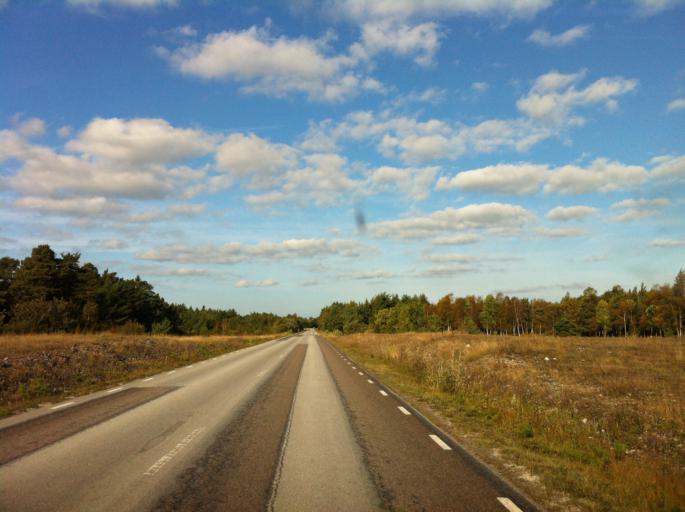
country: SE
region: Gotland
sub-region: Gotland
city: Slite
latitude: 57.4410
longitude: 18.7371
